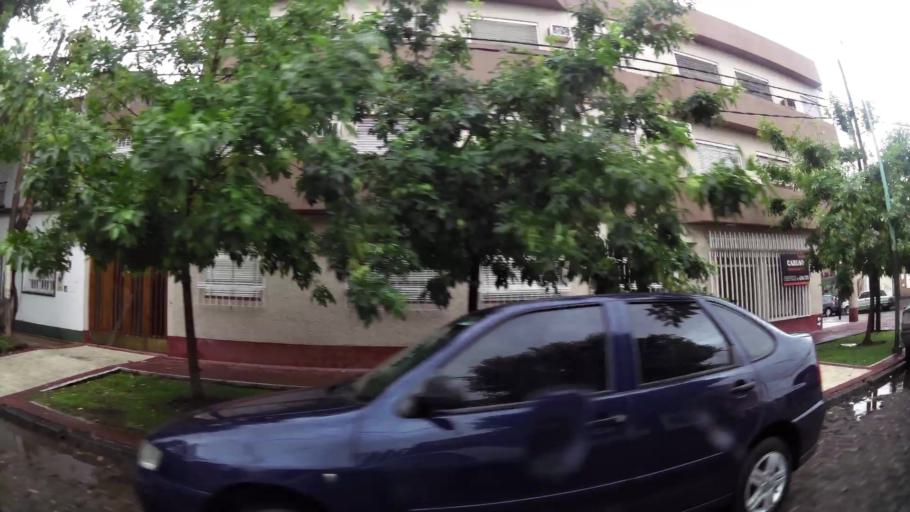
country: AR
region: Buenos Aires
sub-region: Partido de Lomas de Zamora
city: Lomas de Zamora
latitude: -34.7440
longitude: -58.3858
